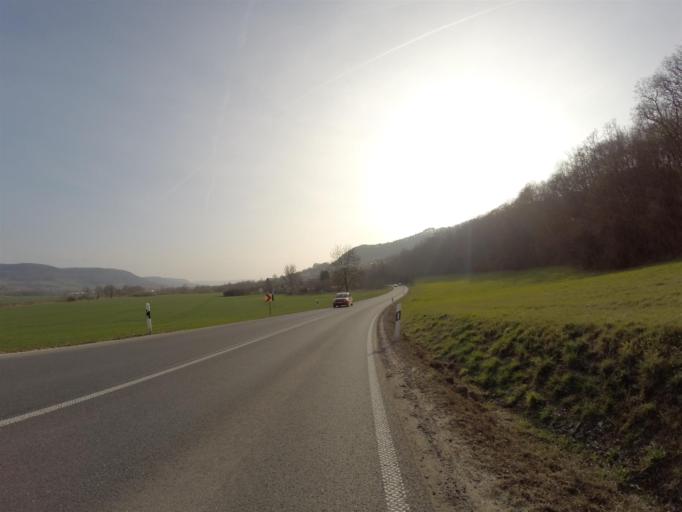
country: DE
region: Thuringia
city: Neuengonna
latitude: 50.9694
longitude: 11.6304
